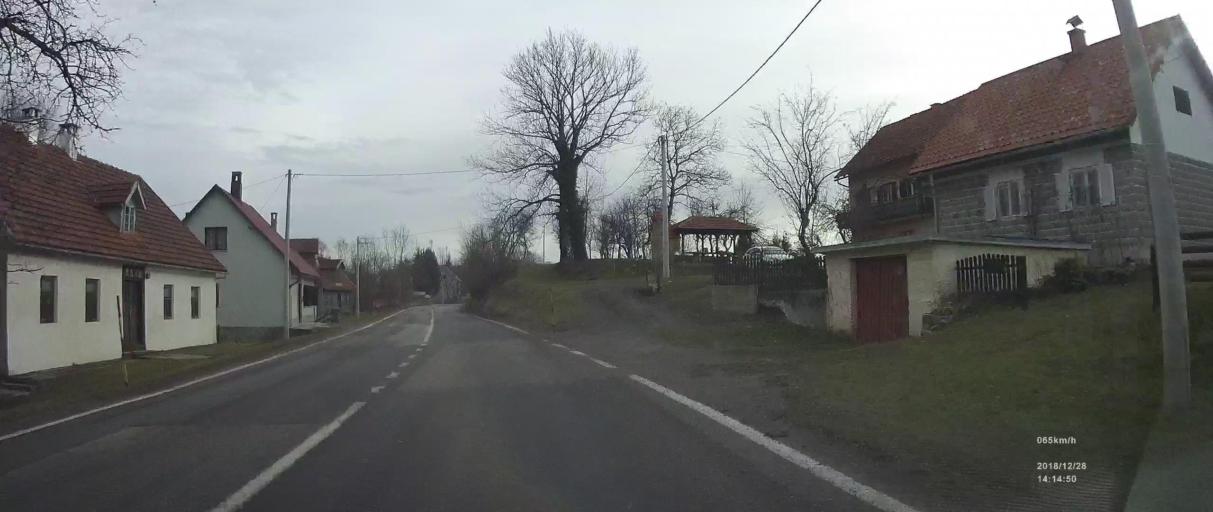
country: HR
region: Primorsko-Goranska
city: Vrbovsko
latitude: 45.4289
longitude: 15.0226
